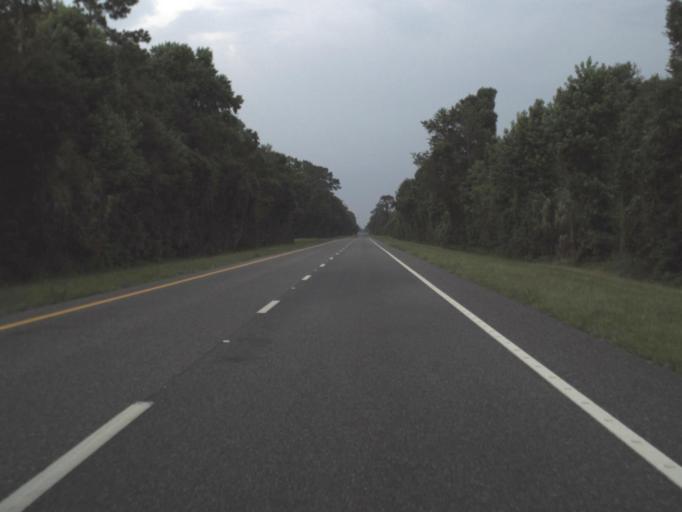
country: US
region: Florida
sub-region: Levy County
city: Inglis
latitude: 29.1796
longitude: -82.6694
